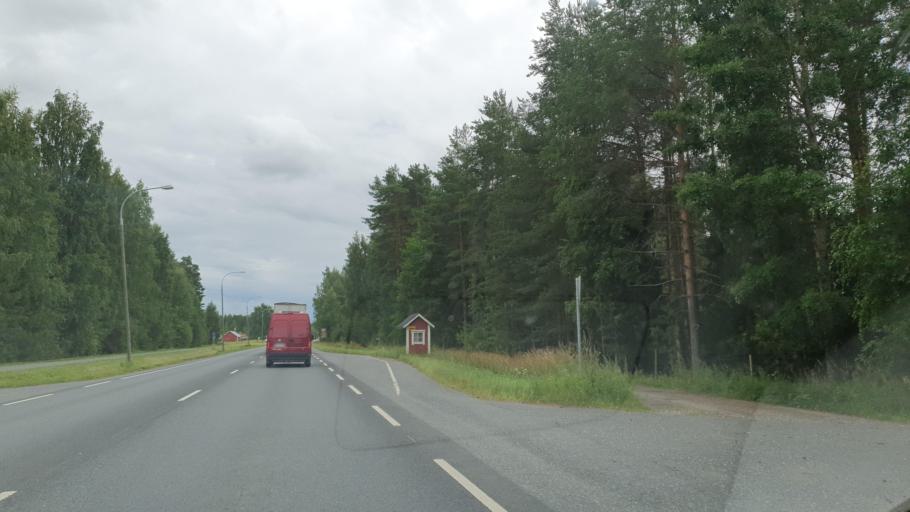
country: FI
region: Northern Savo
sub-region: Ylae-Savo
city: Lapinlahti
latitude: 63.4657
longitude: 27.3081
